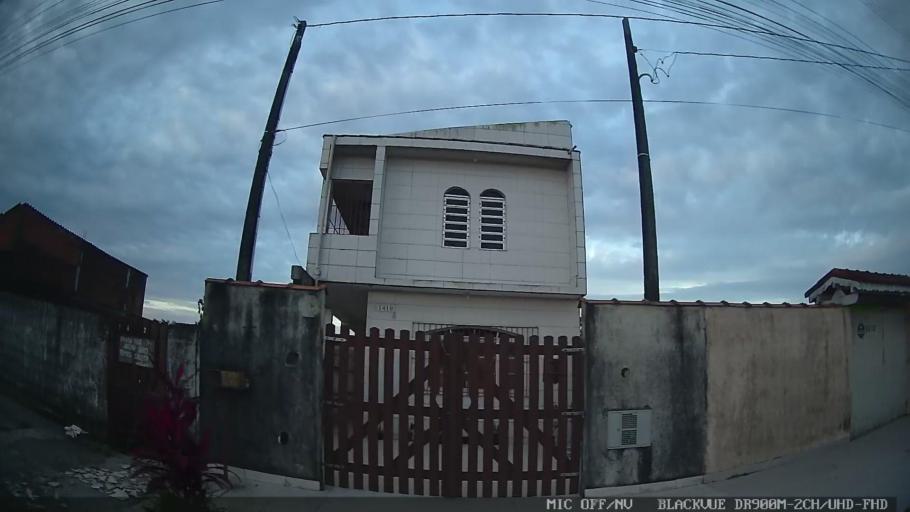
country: BR
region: Sao Paulo
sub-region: Itanhaem
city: Itanhaem
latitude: -24.1697
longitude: -46.7817
